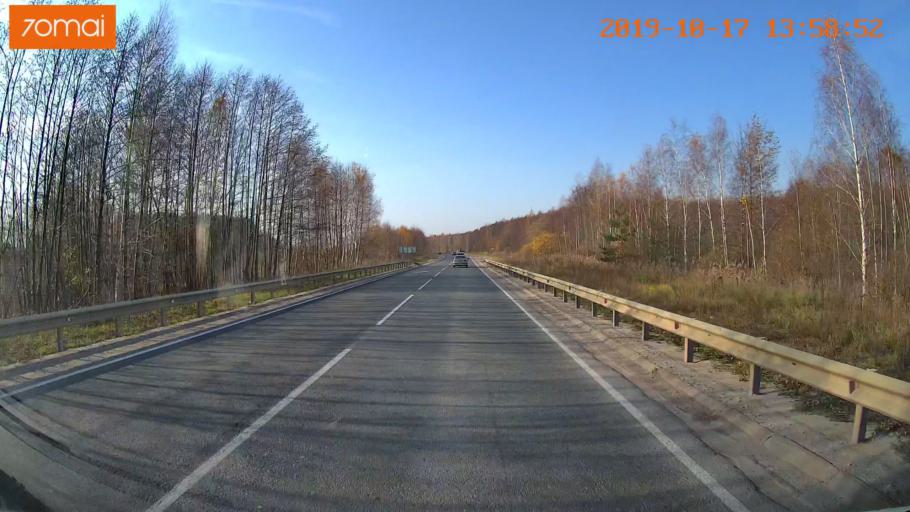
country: RU
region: Rjazan
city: Spas-Klepiki
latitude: 55.1402
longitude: 40.2157
